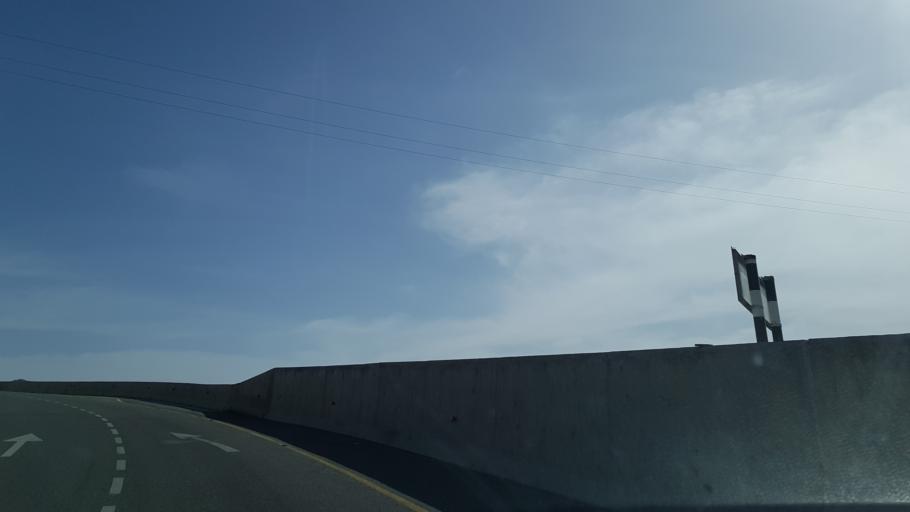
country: OM
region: Muhafazat ad Dakhiliyah
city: Izki
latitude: 23.0719
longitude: 57.7119
